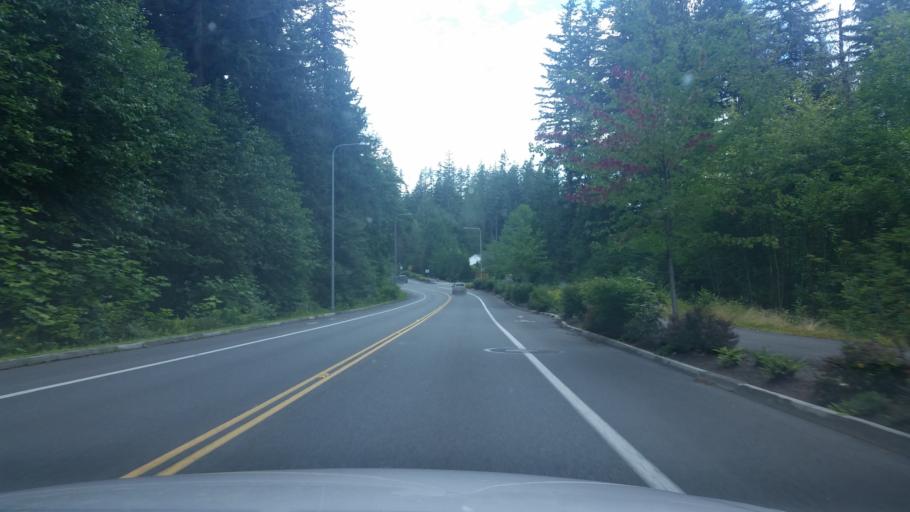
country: US
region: Washington
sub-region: King County
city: Union Hill-Novelty Hill
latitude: 47.7148
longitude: -122.0268
